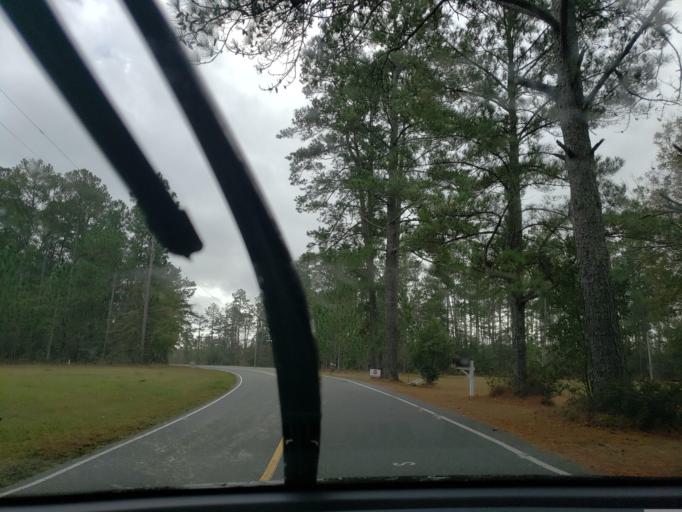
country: US
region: North Carolina
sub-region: Onslow County
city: Richlands
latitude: 34.7273
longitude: -77.6266
